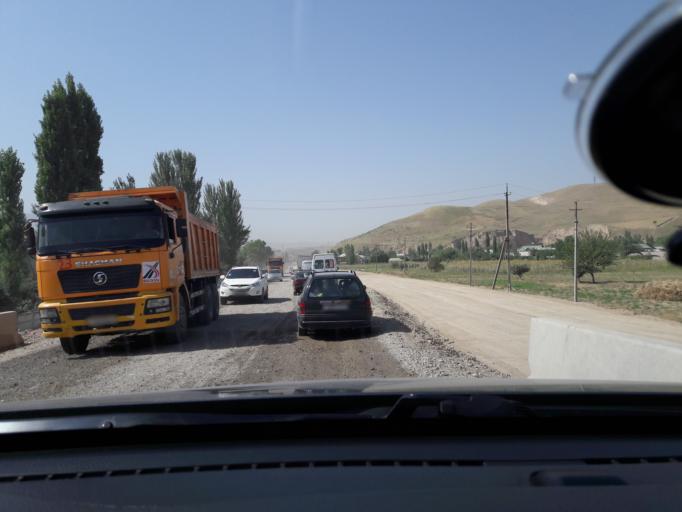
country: TJ
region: Dushanbe
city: Boshkengash
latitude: 38.4490
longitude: 68.7341
